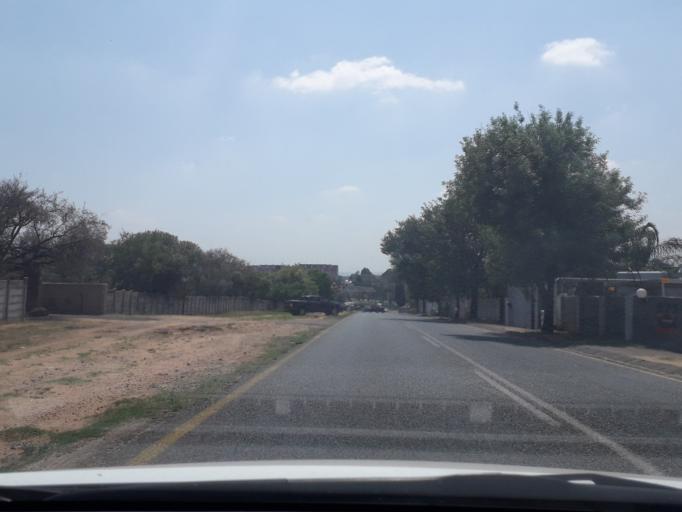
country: ZA
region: Gauteng
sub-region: West Rand District Municipality
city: Muldersdriseloop
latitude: -26.0732
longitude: 27.9339
